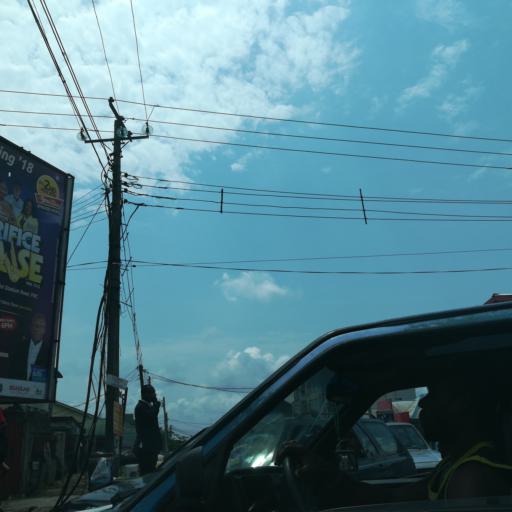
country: NG
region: Rivers
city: Port Harcourt
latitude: 4.8053
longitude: 7.0039
